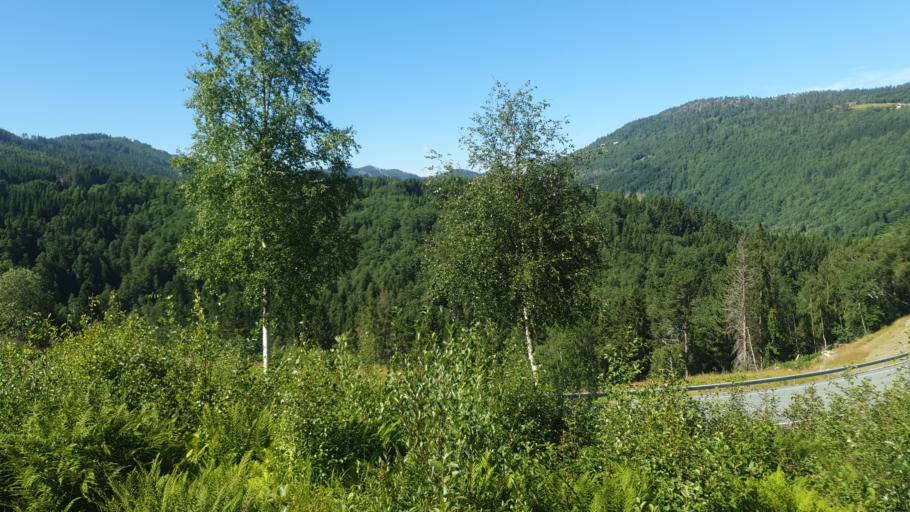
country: NO
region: Sor-Trondelag
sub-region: Meldal
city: Meldal
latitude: 63.1571
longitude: 9.7263
